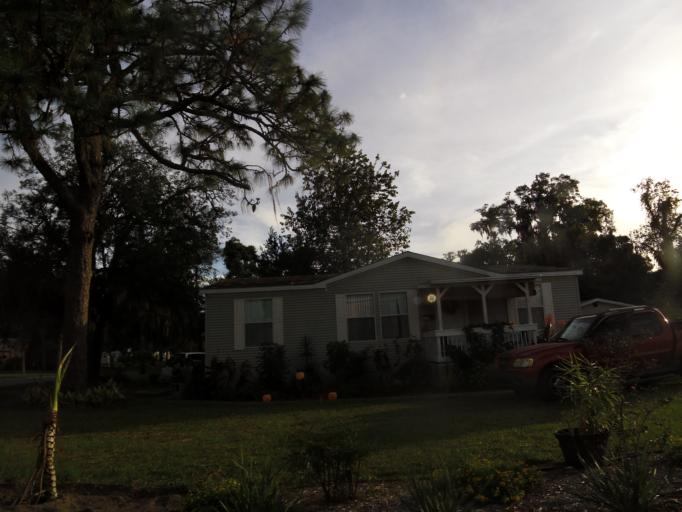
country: US
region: Florida
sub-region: Duval County
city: Jacksonville
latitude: 30.3878
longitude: -81.6571
